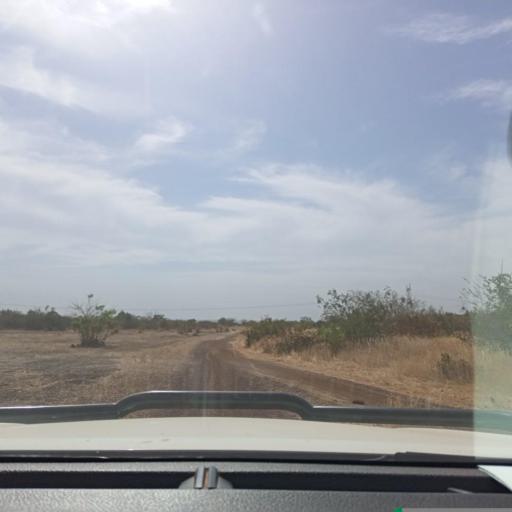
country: ML
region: Koulikoro
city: Kati
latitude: 12.7373
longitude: -8.2499
